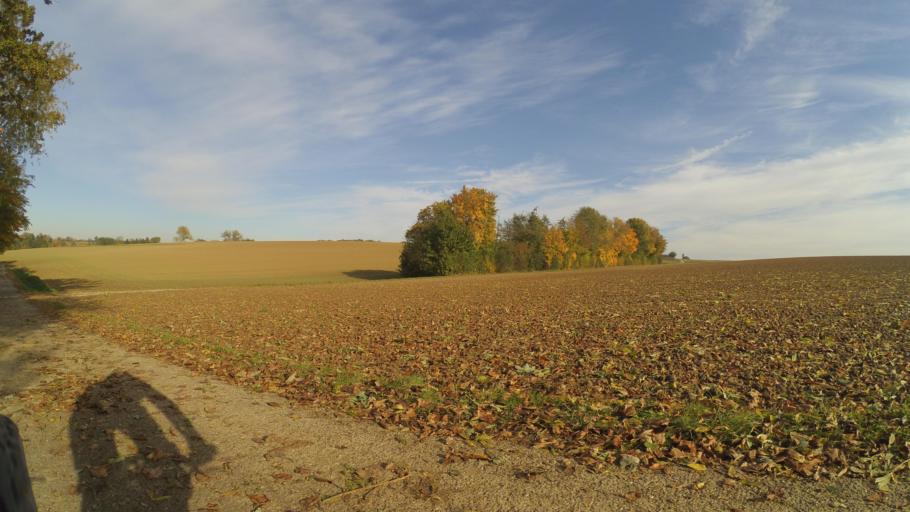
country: DE
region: Baden-Wuerttemberg
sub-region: Regierungsbezirk Stuttgart
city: Neuenstein
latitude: 49.2020
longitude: 9.5522
